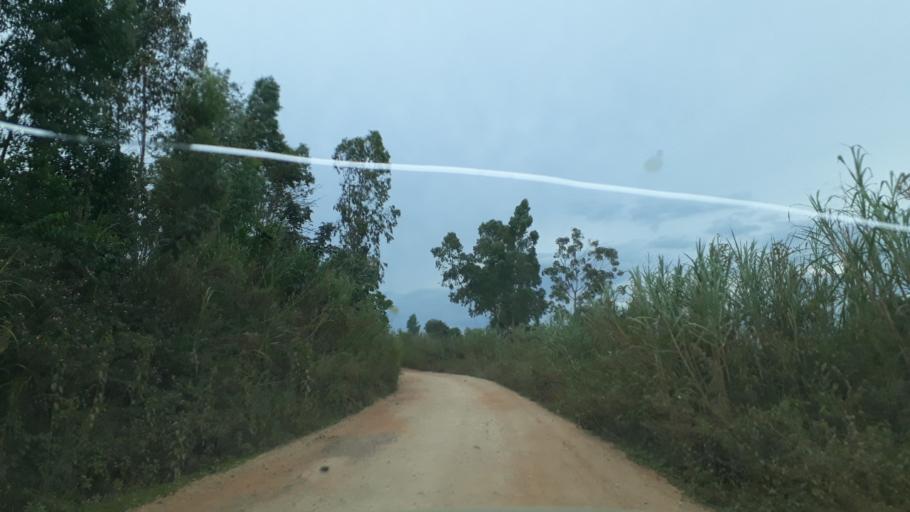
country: CD
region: Eastern Province
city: Bunia
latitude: 1.9116
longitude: 30.5069
